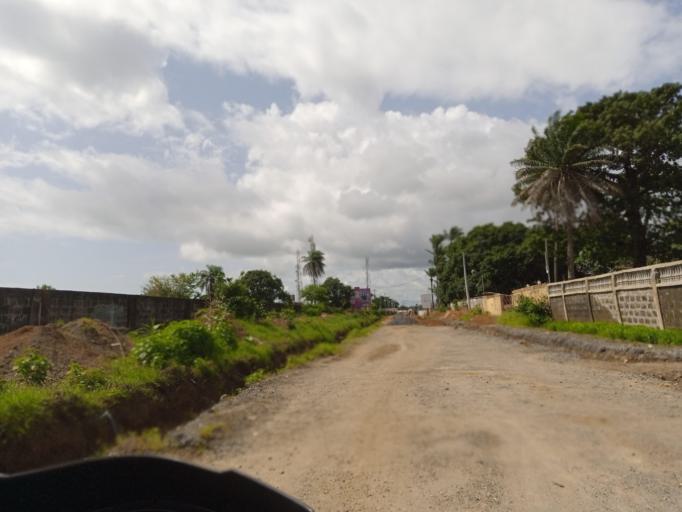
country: SL
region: Northern Province
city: Masoyila
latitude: 8.6115
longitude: -13.2051
